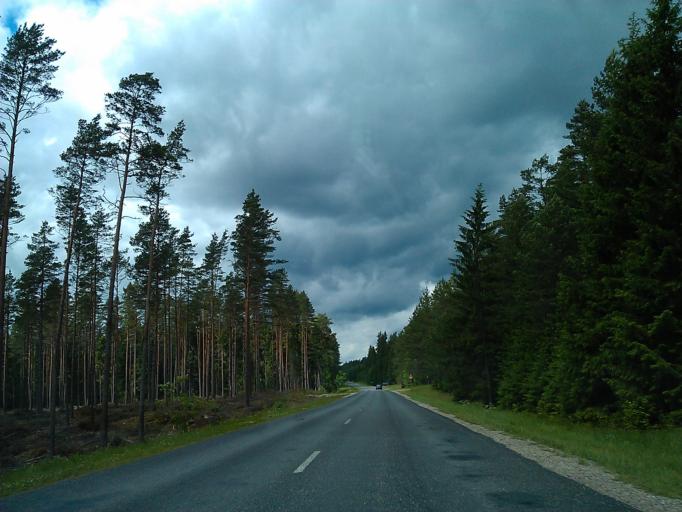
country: LV
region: Talsu Rajons
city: Stende
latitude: 57.0853
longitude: 22.4217
